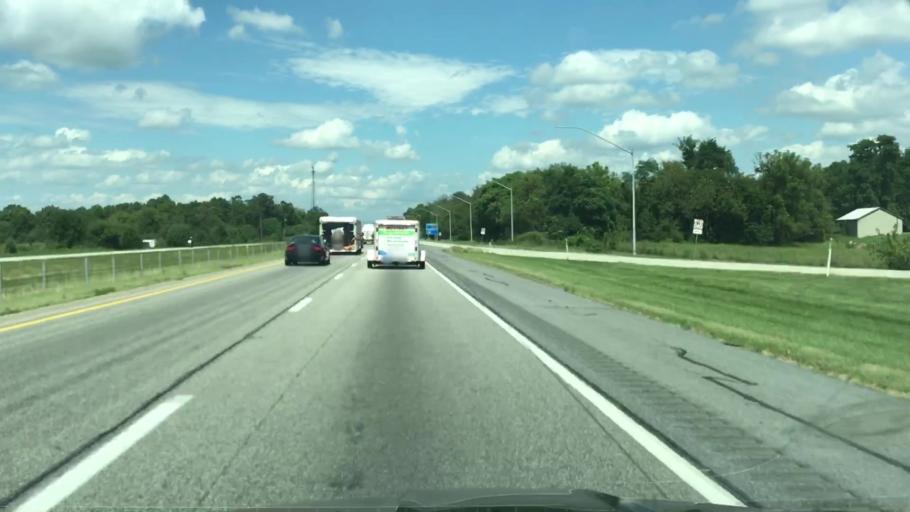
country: US
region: Pennsylvania
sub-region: Franklin County
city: State Line
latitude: 39.7377
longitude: -77.7272
